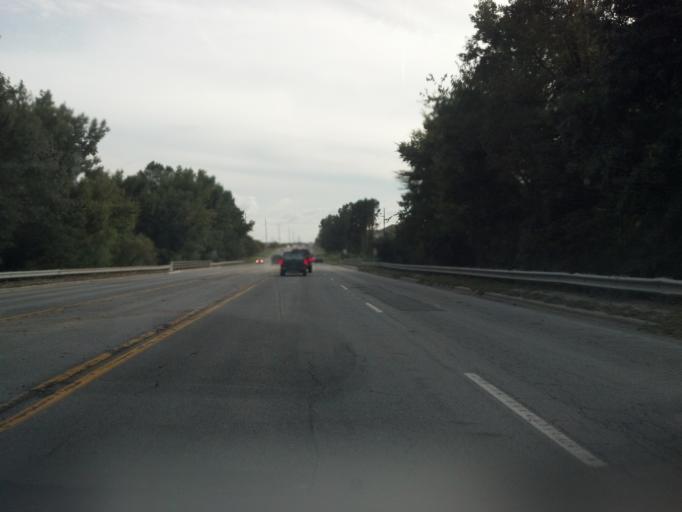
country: US
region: North Carolina
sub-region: Pitt County
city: Greenville
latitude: 35.6065
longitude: -77.3308
